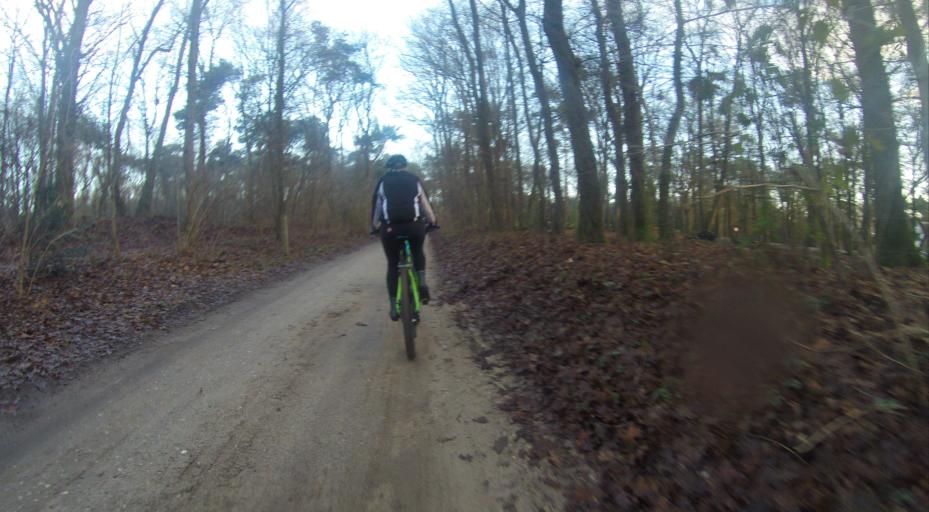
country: NL
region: Overijssel
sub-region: Gemeente Hof van Twente
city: Markelo
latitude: 52.2899
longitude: 6.4227
